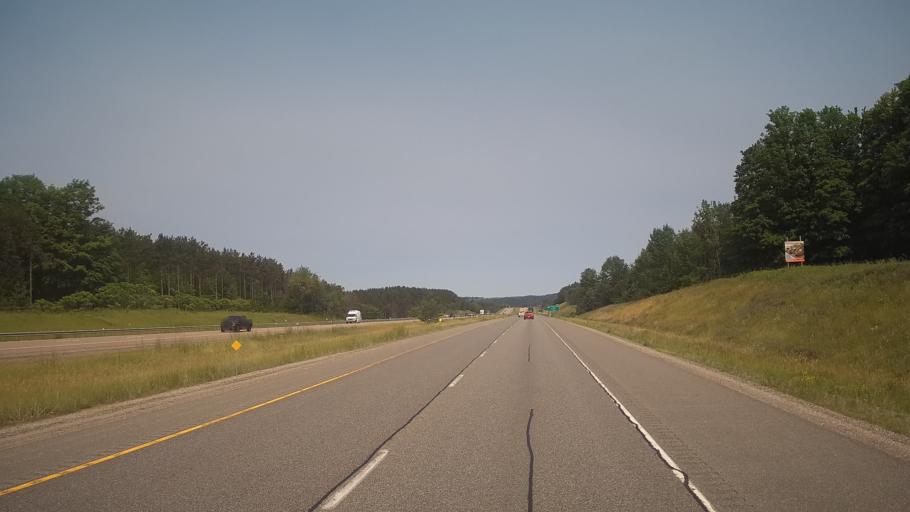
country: CA
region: Ontario
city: Barrie
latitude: 44.5087
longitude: -79.7258
